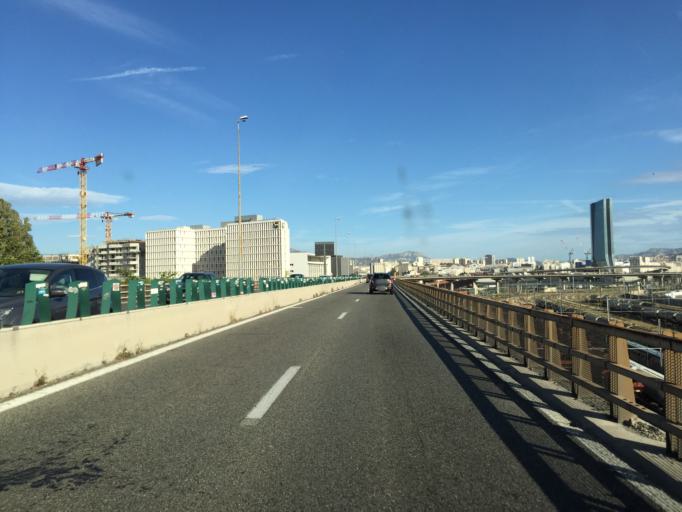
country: FR
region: Provence-Alpes-Cote d'Azur
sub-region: Departement des Bouches-du-Rhone
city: Marseille 03
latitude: 43.3251
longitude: 5.3615
